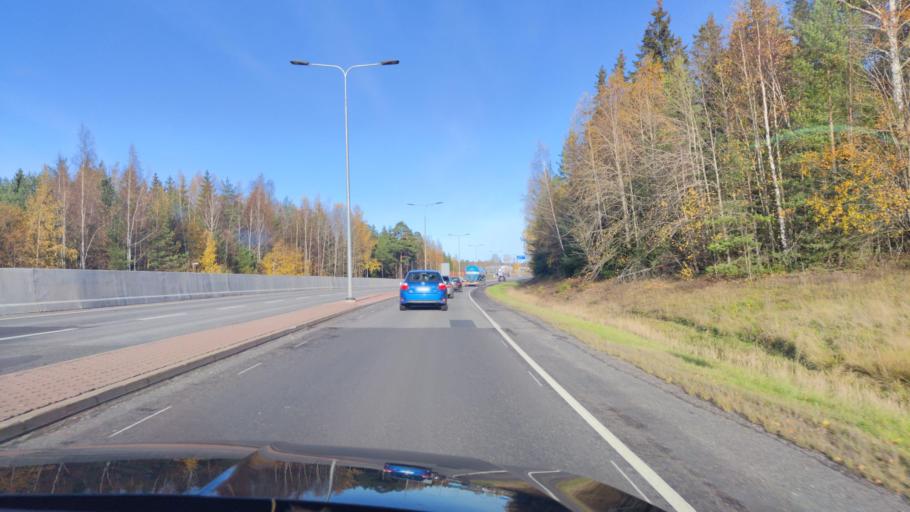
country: FI
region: Varsinais-Suomi
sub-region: Turku
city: Kaarina
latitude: 60.4259
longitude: 22.3806
